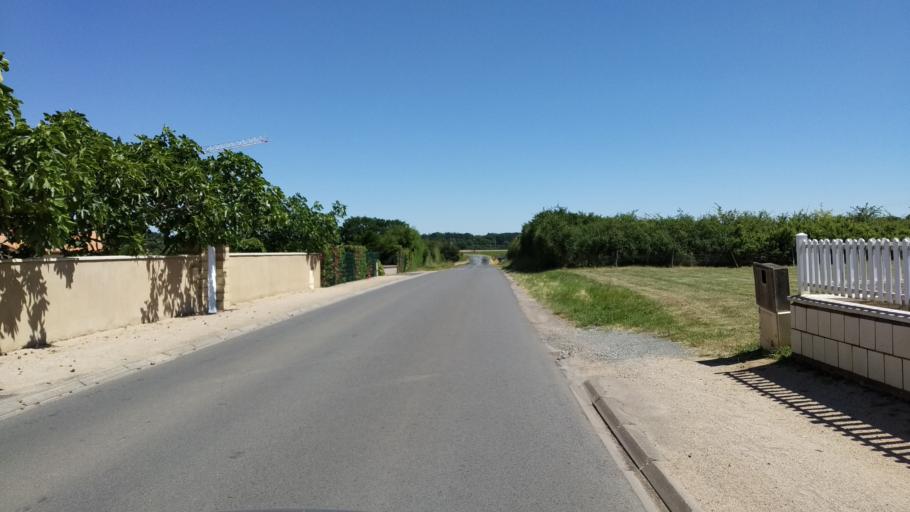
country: FR
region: Poitou-Charentes
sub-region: Departement de la Vienne
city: Biard
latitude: 46.6018
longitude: 0.2875
